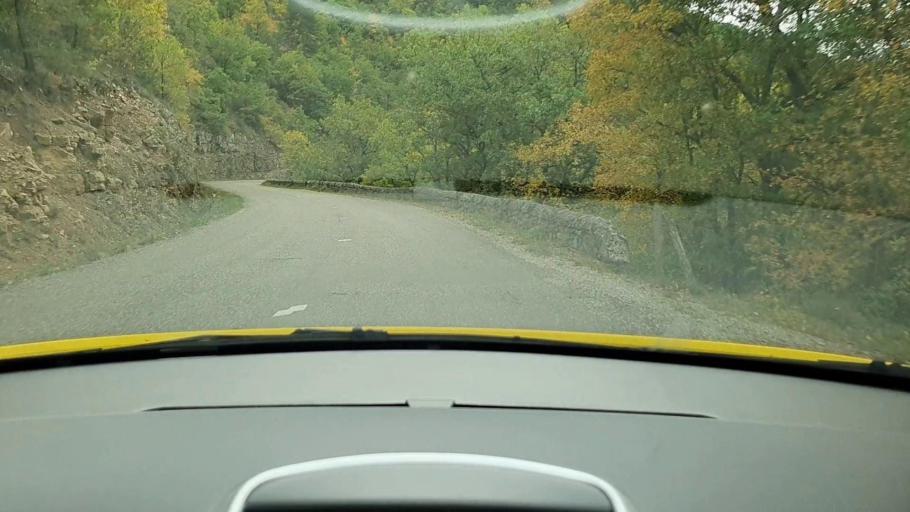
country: FR
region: Languedoc-Roussillon
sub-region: Departement de la Lozere
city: Meyrueis
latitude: 44.0764
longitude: 3.3396
